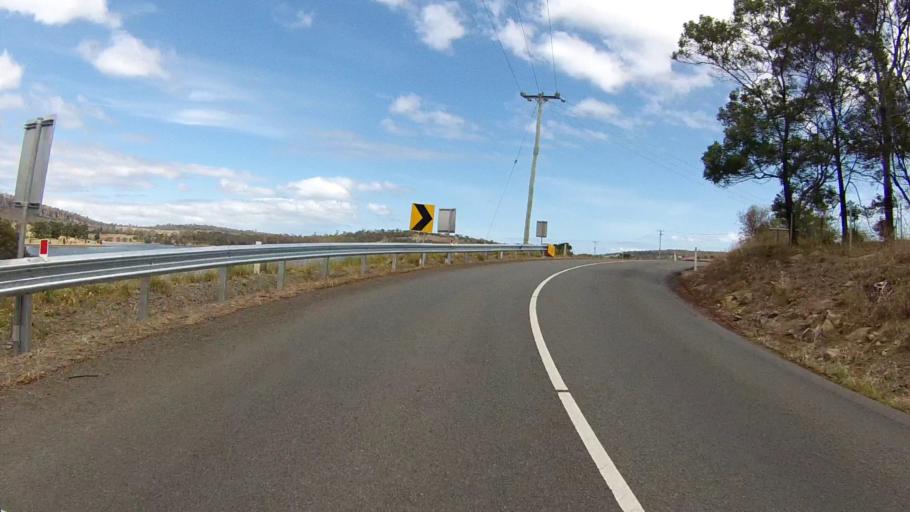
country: AU
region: Tasmania
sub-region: Sorell
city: Sorell
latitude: -42.8644
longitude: 147.6776
